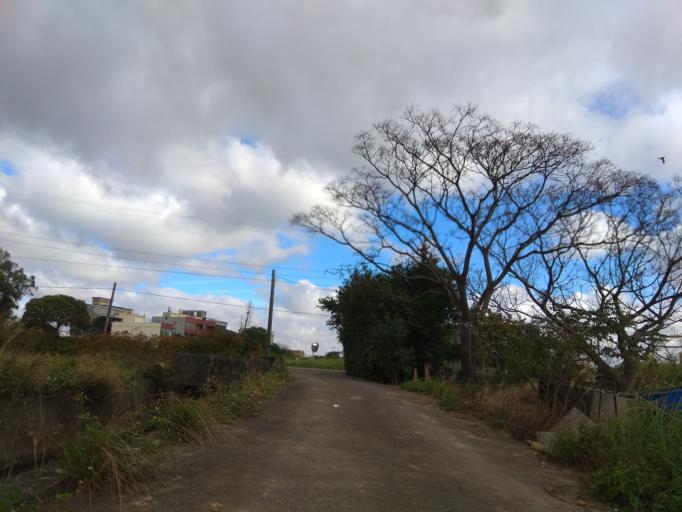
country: TW
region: Taiwan
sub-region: Hsinchu
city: Zhubei
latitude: 24.9715
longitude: 121.0858
